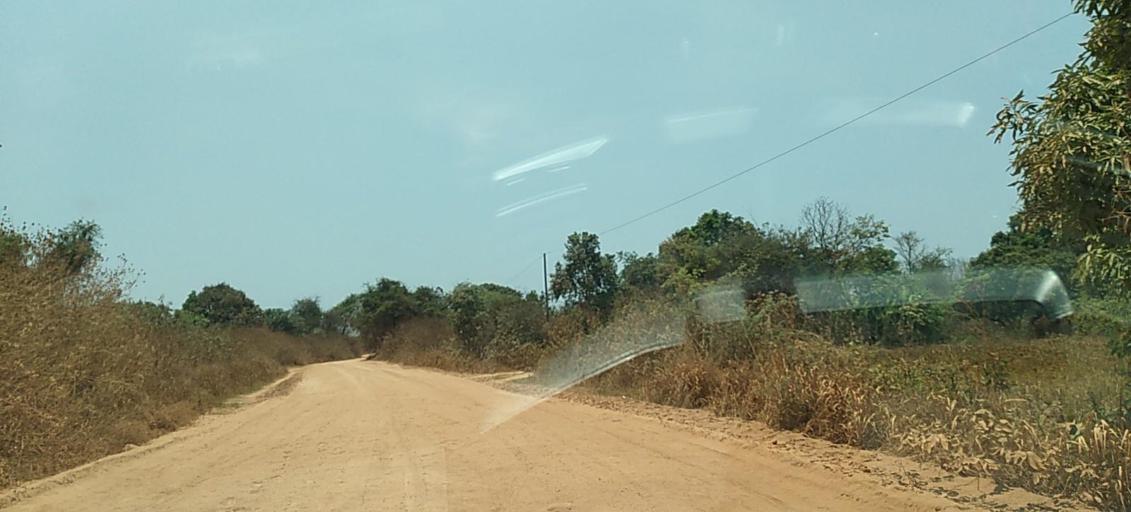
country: CD
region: Katanga
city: Kipushi
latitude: -11.7816
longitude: 27.1836
